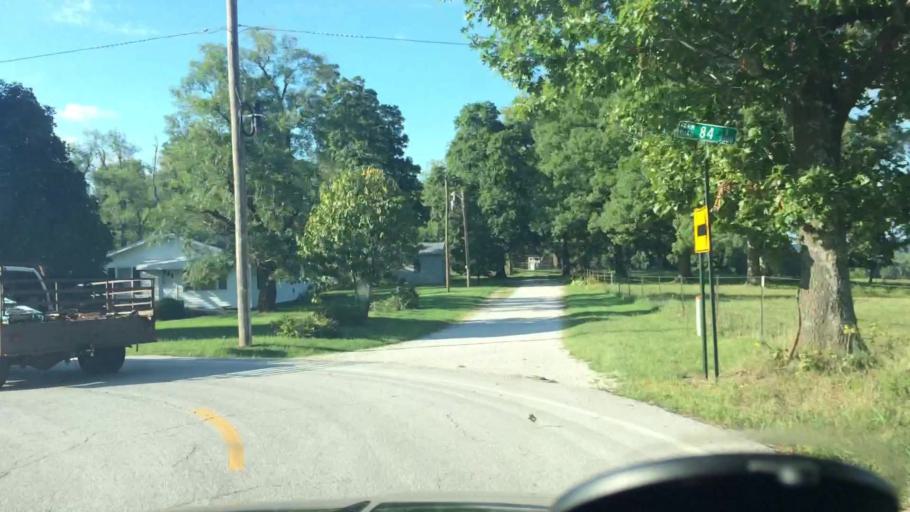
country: US
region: Missouri
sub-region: Greene County
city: Strafford
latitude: 37.2845
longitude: -93.0811
